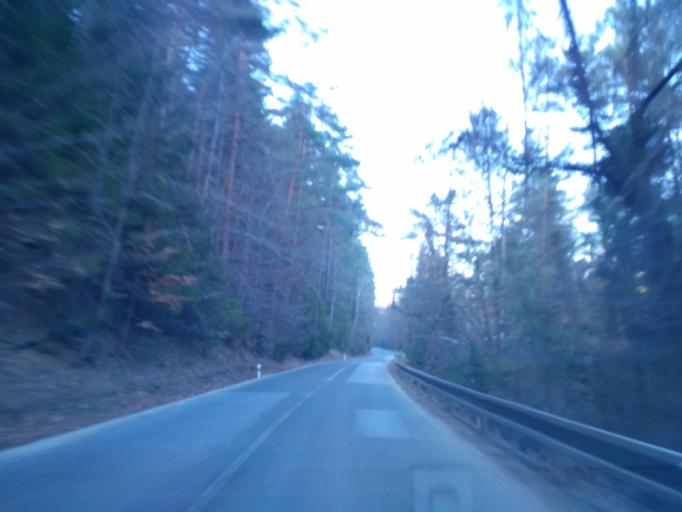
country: SK
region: Kosicky
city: Medzev
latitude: 48.7679
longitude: 20.7805
